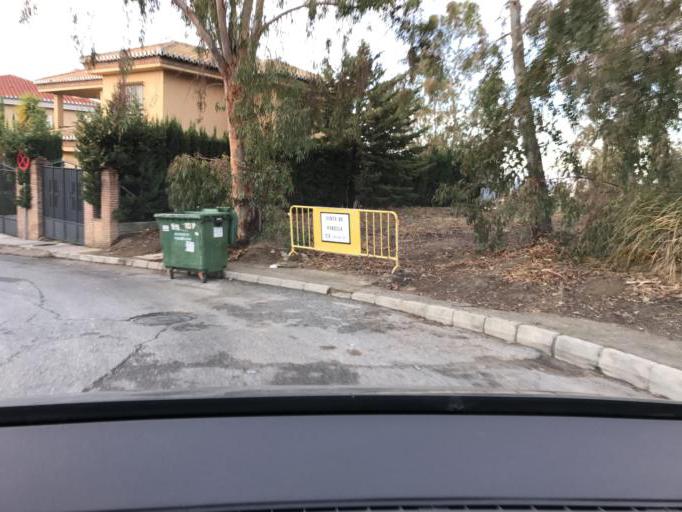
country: ES
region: Andalusia
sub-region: Provincia de Granada
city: Cenes de la Vega
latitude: 37.1653
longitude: -3.5418
